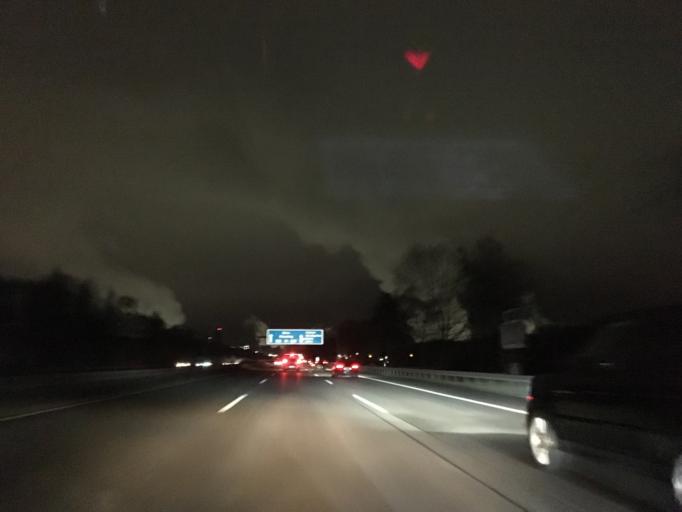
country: DE
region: North Rhine-Westphalia
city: Wesseling
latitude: 50.8563
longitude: 6.9686
